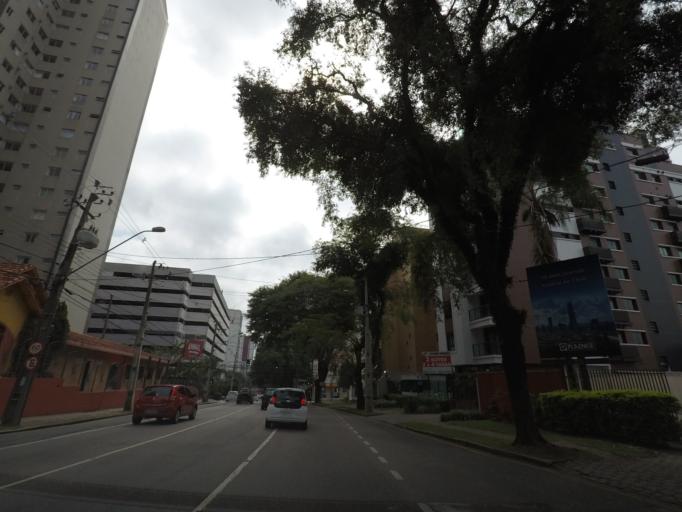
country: BR
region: Parana
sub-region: Curitiba
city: Curitiba
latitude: -25.4520
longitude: -49.2845
